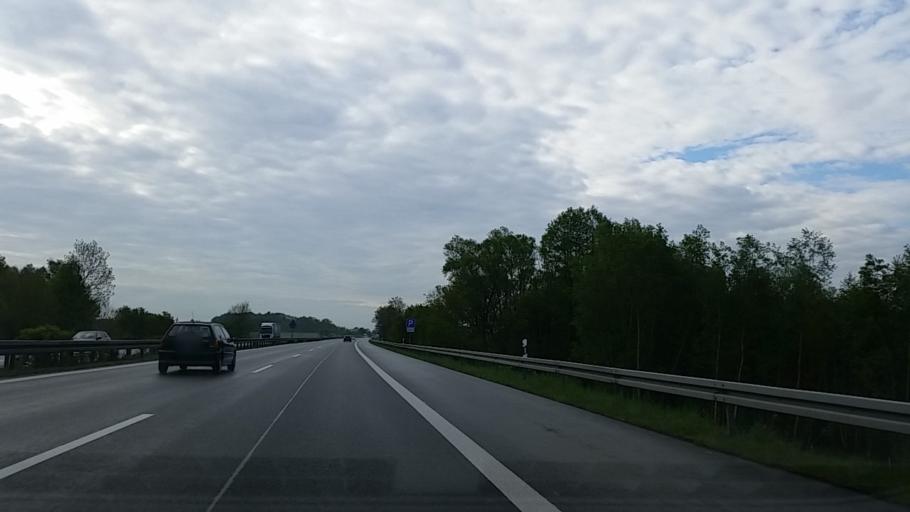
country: DE
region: Brandenburg
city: Gerdshagen
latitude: 53.2024
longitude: 12.2668
